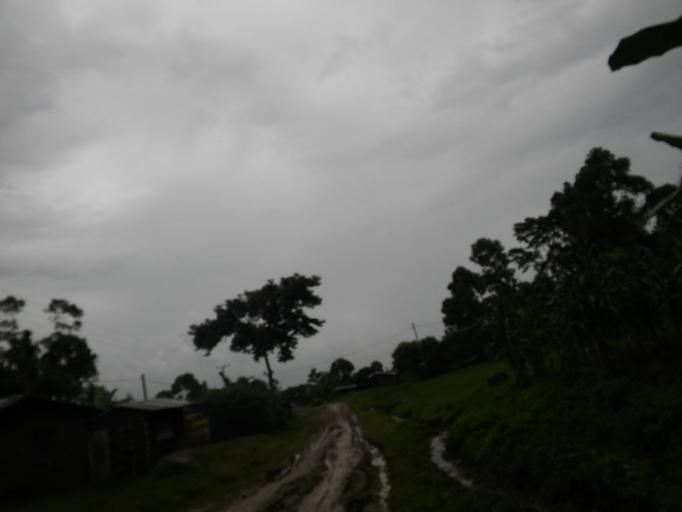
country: UG
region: Eastern Region
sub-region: Bududa District
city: Bududa
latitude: 1.0042
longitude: 34.2455
